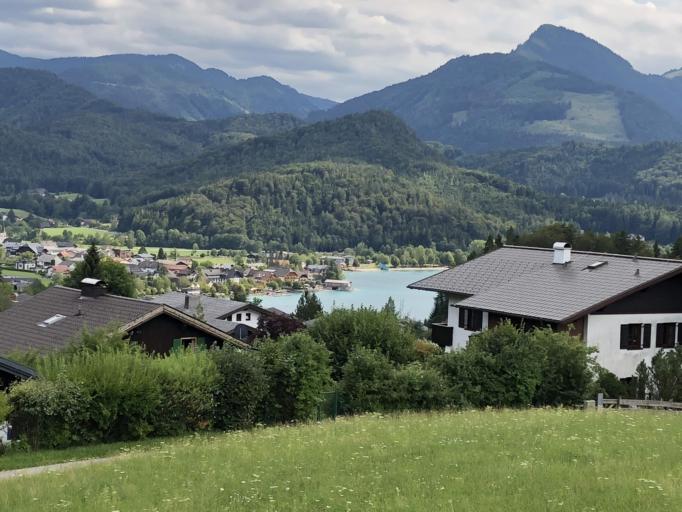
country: AT
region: Salzburg
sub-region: Politischer Bezirk Salzburg-Umgebung
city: Fuschl am See
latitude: 47.8067
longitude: 13.2943
